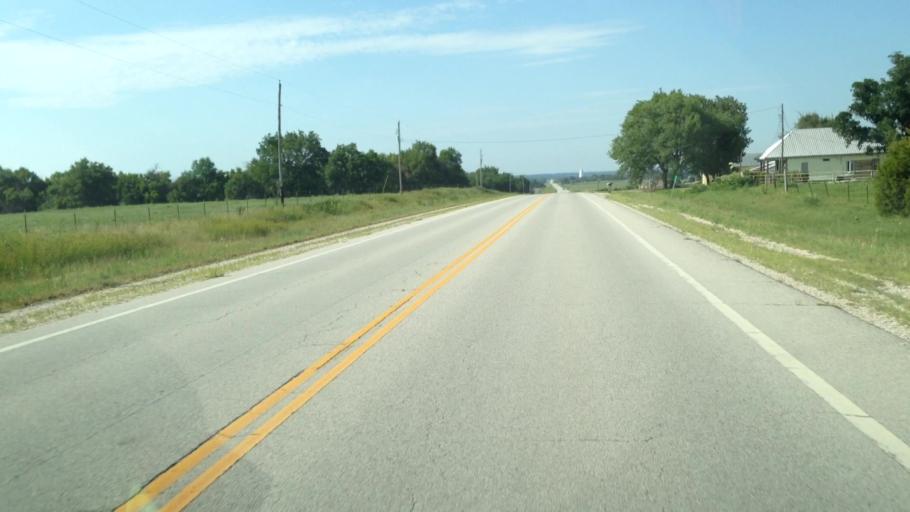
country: US
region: Kansas
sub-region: Neosho County
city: Erie
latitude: 37.4762
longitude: -95.2692
